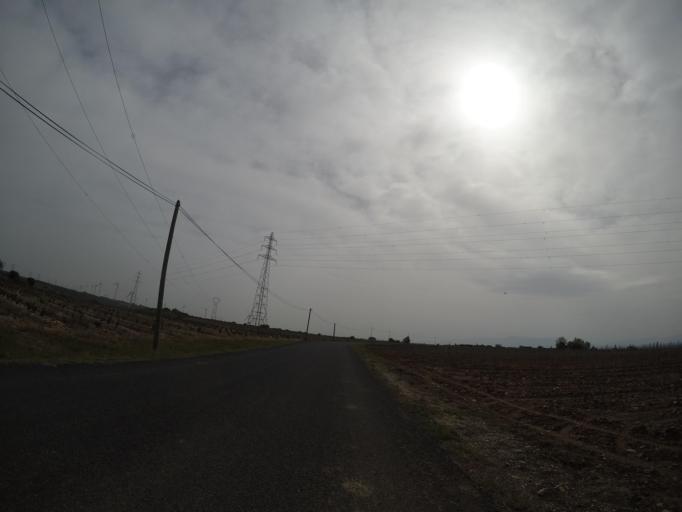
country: FR
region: Languedoc-Roussillon
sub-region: Departement des Pyrenees-Orientales
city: Pezilla-la-Riviere
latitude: 42.7137
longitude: 2.7557
